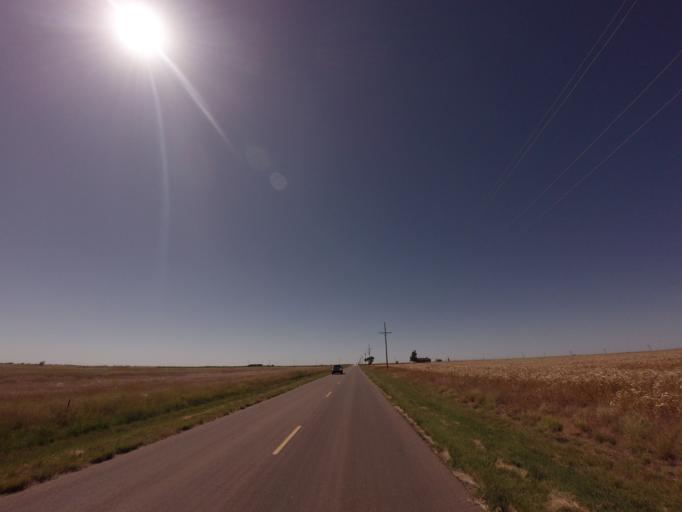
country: US
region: New Mexico
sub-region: Curry County
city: Clovis
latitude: 34.4485
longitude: -103.2191
